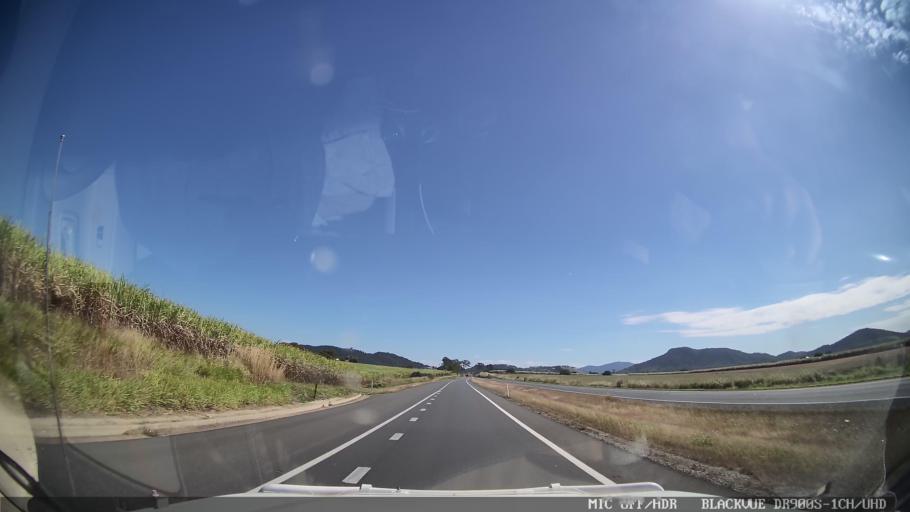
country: AU
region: Queensland
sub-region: Mackay
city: Walkerston
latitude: -21.0914
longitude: 149.0572
